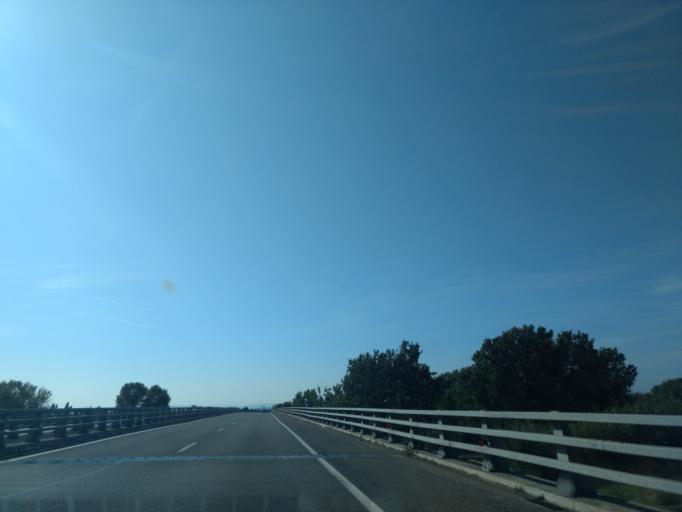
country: ES
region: Catalonia
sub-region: Provincia de Girona
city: Castello d'Empuries
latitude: 42.2552
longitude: 3.0871
